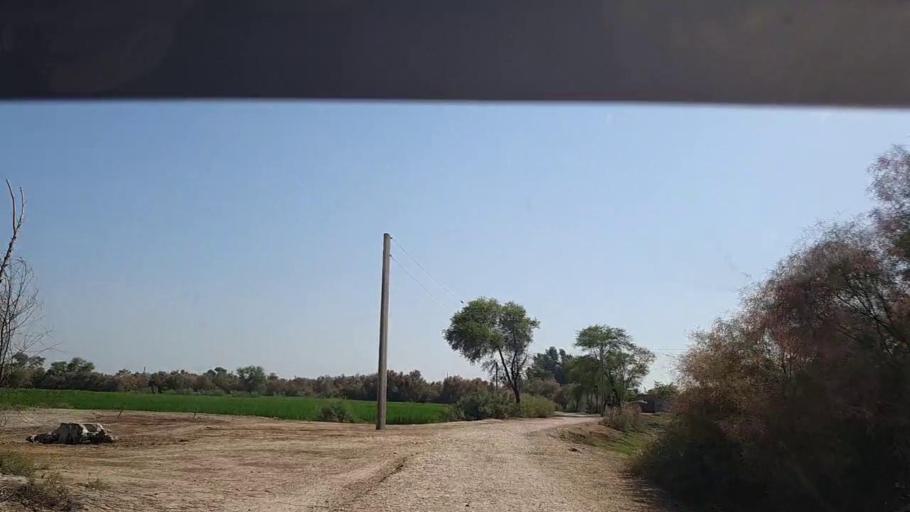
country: PK
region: Sindh
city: Ghauspur
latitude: 28.2084
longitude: 69.0779
